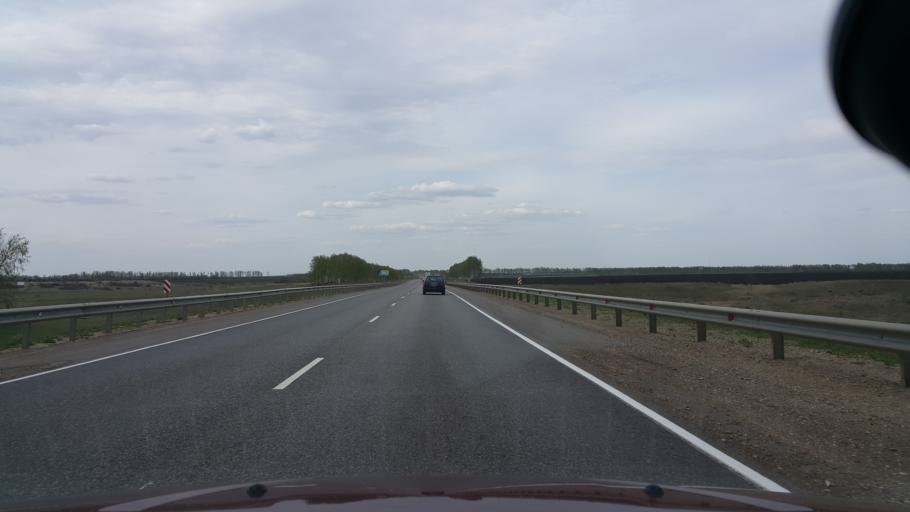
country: RU
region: Tambov
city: Pokrovo-Prigorodnoye
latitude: 52.6451
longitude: 41.3411
